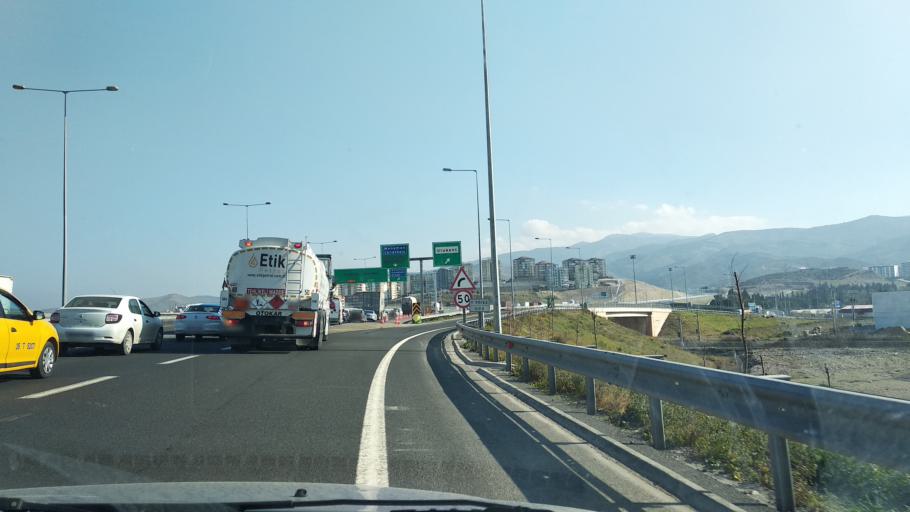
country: TR
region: Izmir
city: Menemen
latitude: 38.5711
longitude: 27.0518
